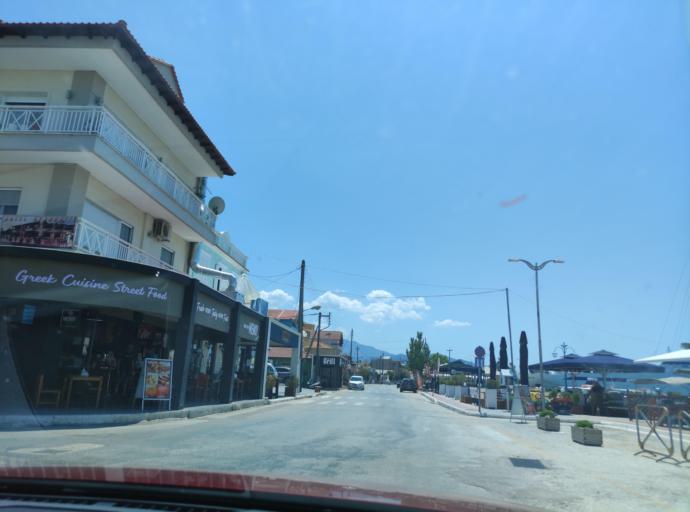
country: GR
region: East Macedonia and Thrace
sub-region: Nomos Kavalas
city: Keramoti
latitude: 40.8583
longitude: 24.7037
